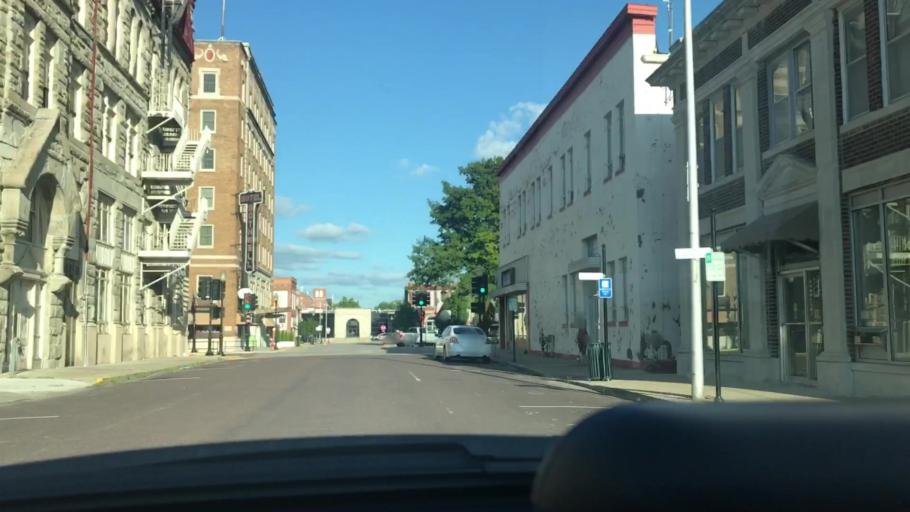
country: US
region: Missouri
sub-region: Pettis County
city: Sedalia
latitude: 38.7078
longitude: -93.2289
